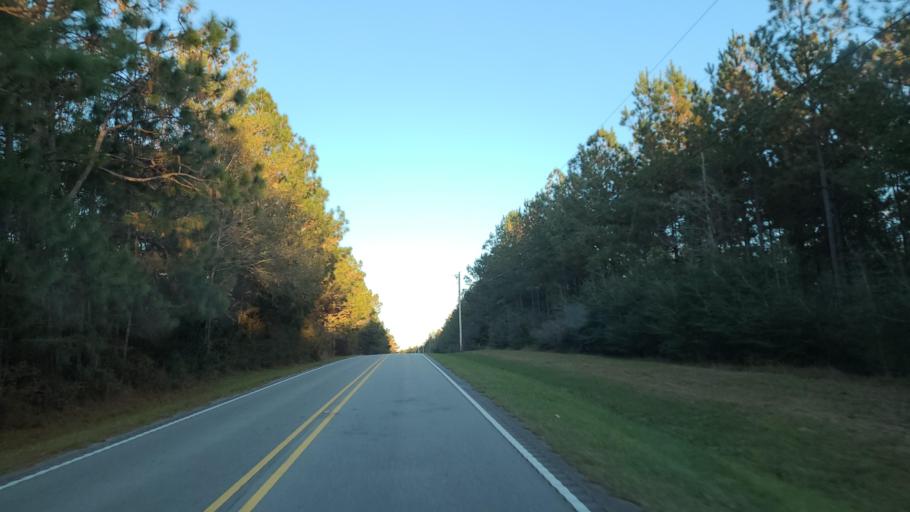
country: US
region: Mississippi
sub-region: Stone County
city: Wiggins
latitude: 31.0263
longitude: -89.2429
